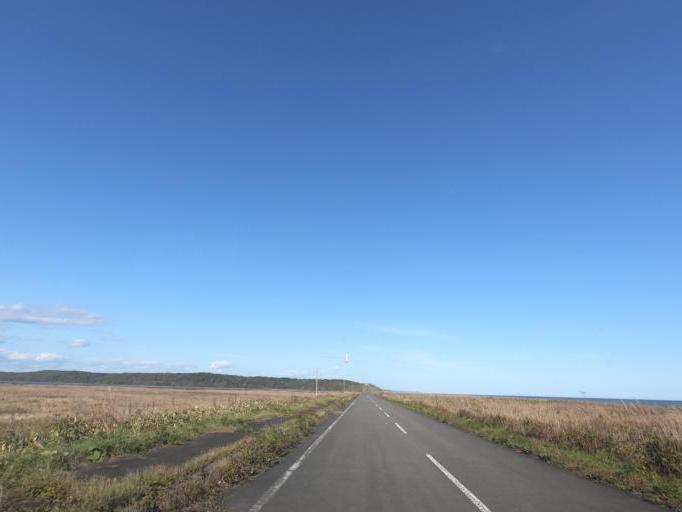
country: JP
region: Hokkaido
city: Obihiro
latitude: 42.5911
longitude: 143.5408
